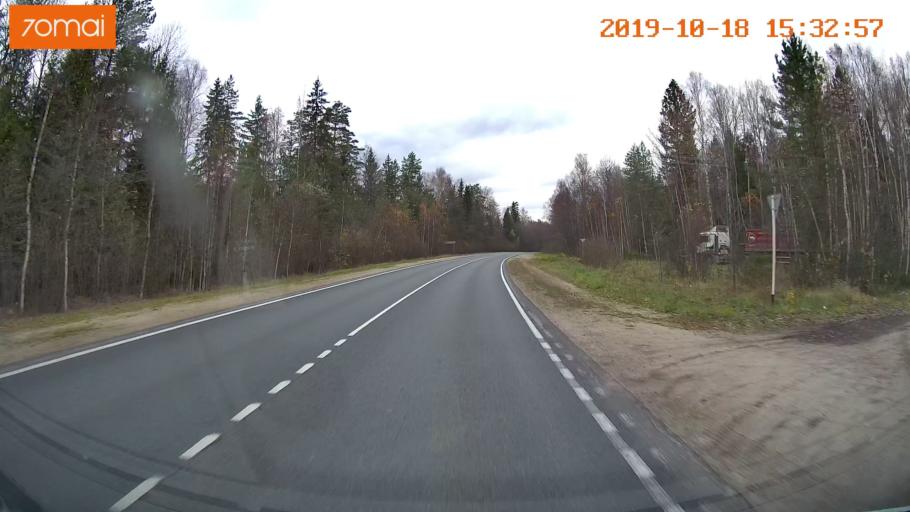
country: RU
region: Vladimir
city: Anopino
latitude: 55.8331
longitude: 40.6448
